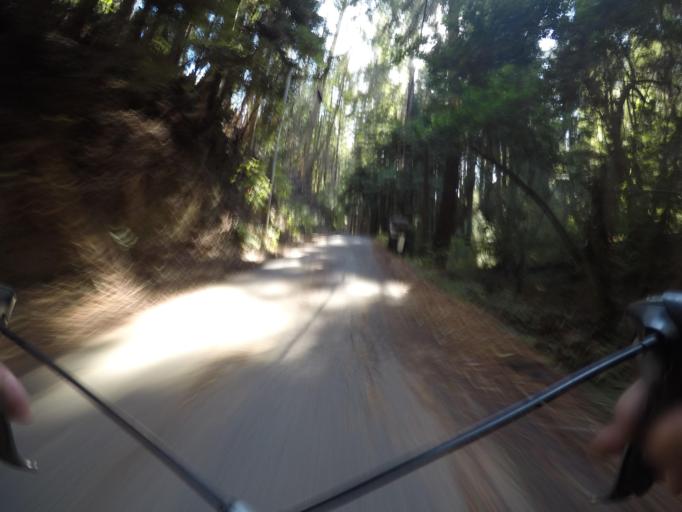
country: US
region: California
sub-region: Santa Cruz County
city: Scotts Valley
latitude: 37.0304
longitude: -122.0088
